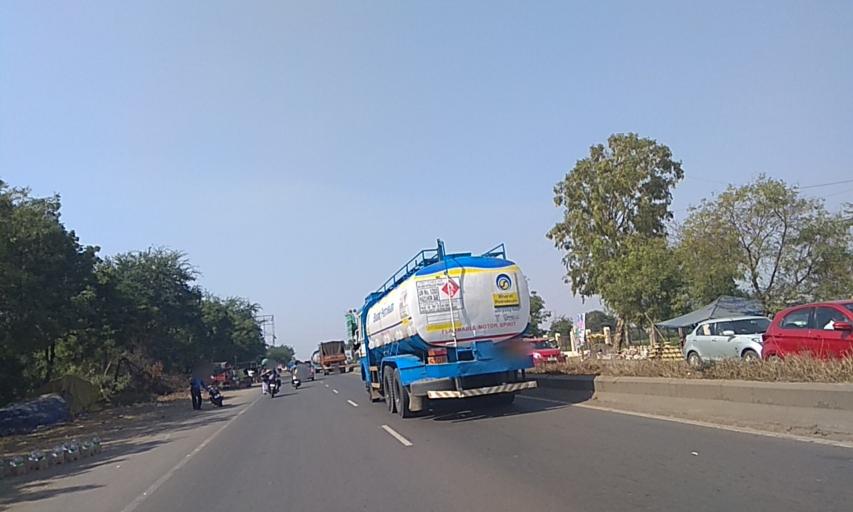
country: IN
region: Maharashtra
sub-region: Pune Division
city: Lohogaon
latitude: 18.4942
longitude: 73.9855
